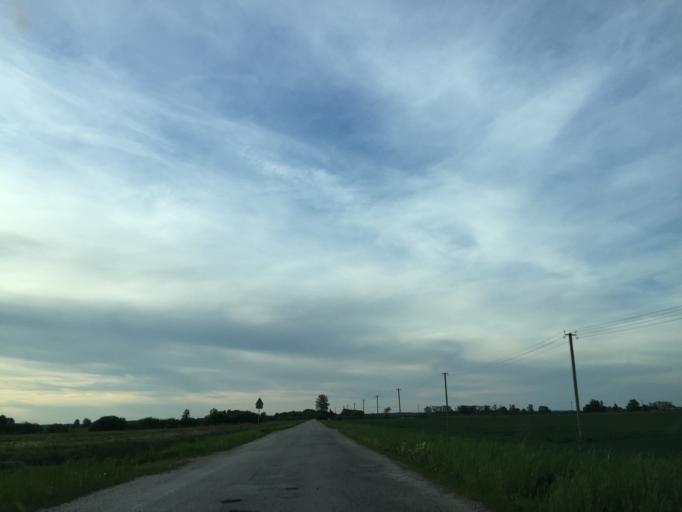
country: LV
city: Tireli
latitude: 56.6947
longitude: 23.5004
